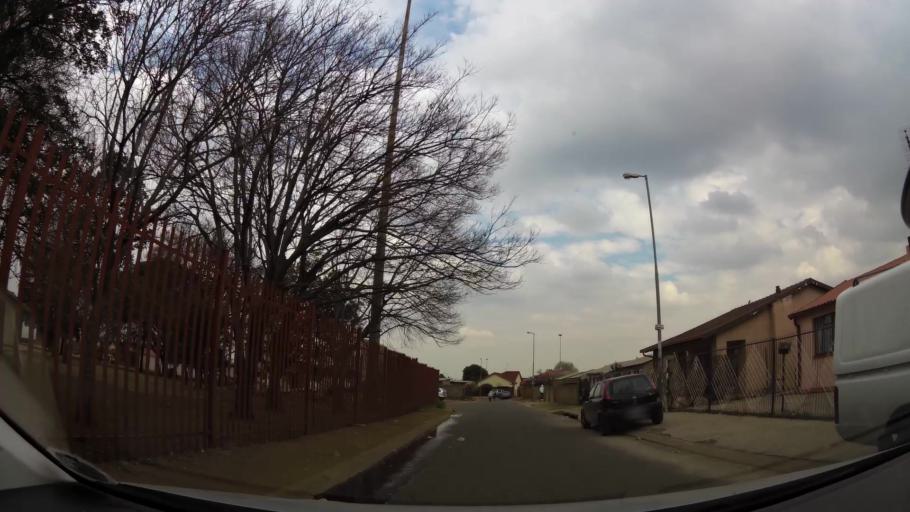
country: ZA
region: Gauteng
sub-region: City of Johannesburg Metropolitan Municipality
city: Soweto
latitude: -26.2607
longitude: 27.8612
